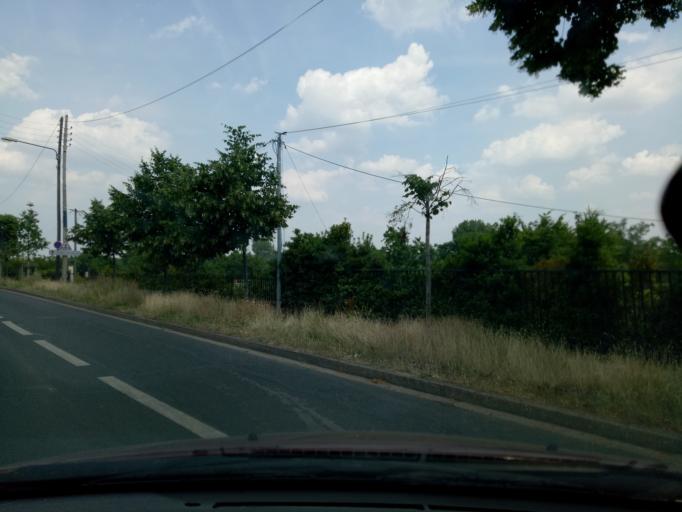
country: FR
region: Ile-de-France
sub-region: Departement des Yvelines
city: Chatou
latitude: 48.8815
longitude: 2.1557
